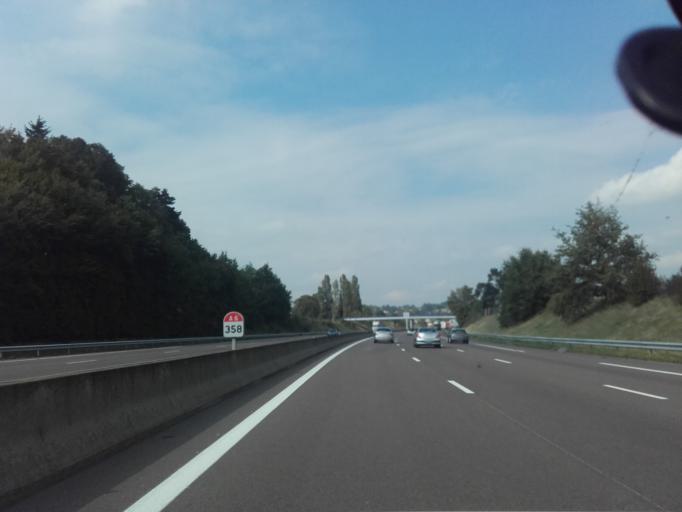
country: FR
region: Bourgogne
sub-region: Departement de Saone-et-Loire
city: Tournus
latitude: 46.5579
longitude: 4.8991
